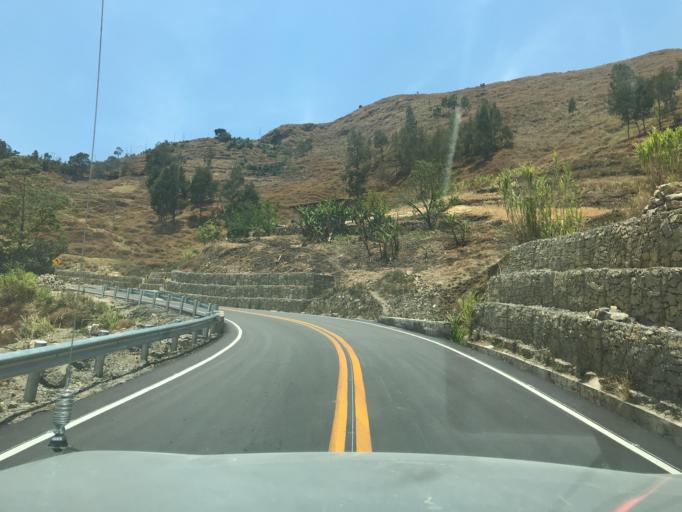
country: TL
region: Manufahi
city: Same
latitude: -8.8788
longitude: 125.5929
